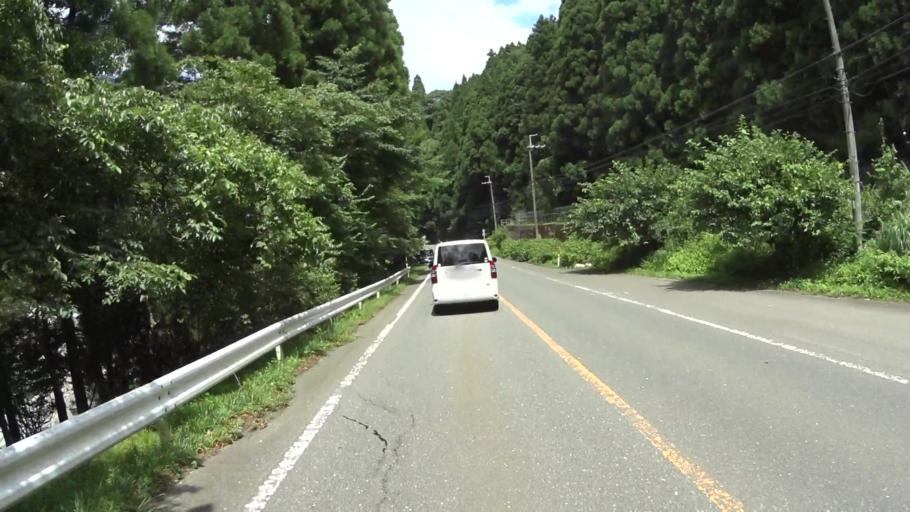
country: JP
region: Shiga Prefecture
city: Kitahama
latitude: 35.2782
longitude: 135.8794
